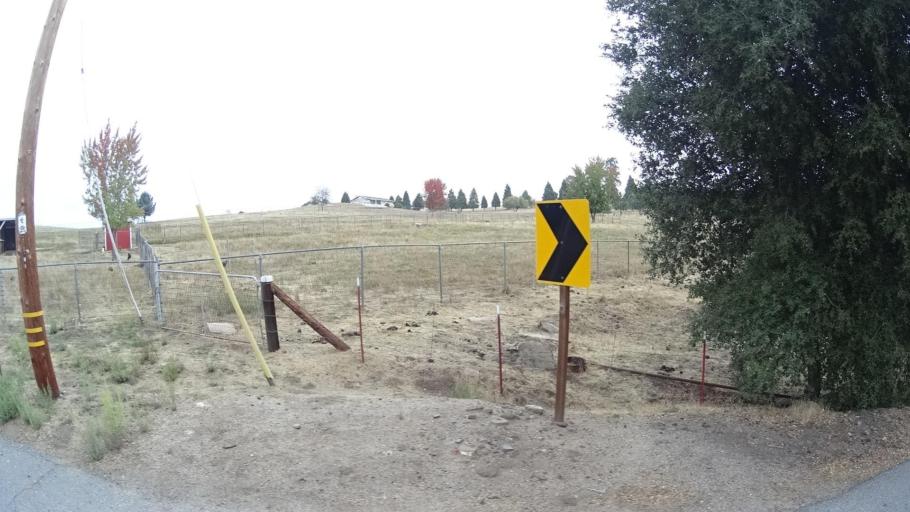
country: US
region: California
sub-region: San Diego County
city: Julian
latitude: 33.0465
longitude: -116.6116
